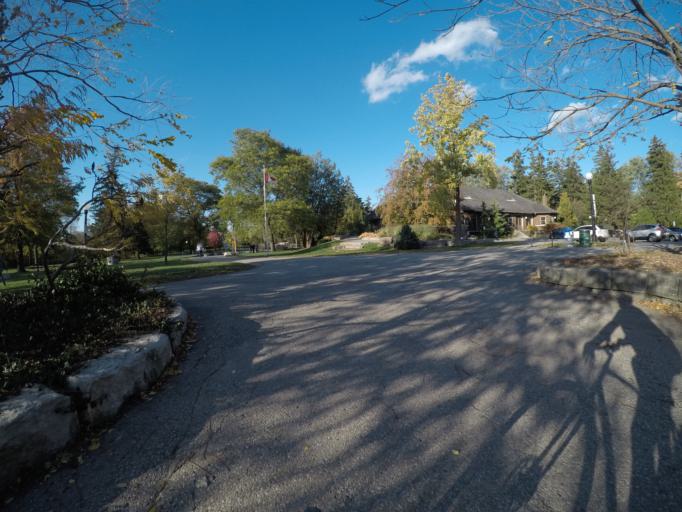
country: CA
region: Ontario
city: Kitchener
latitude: 43.4452
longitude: -80.4995
